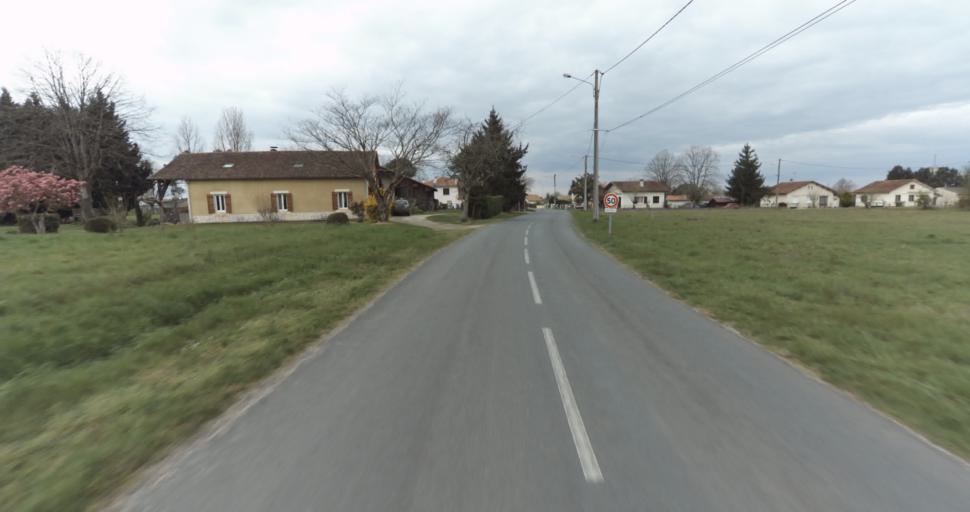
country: FR
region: Aquitaine
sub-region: Departement des Landes
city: Roquefort
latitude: 44.0235
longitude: -0.3278
